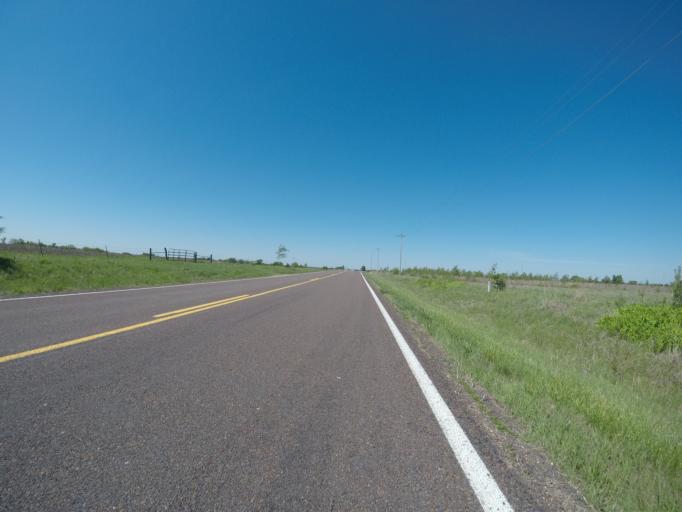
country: US
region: Kansas
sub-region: Osage County
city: Overbrook
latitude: 38.8670
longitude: -95.4615
